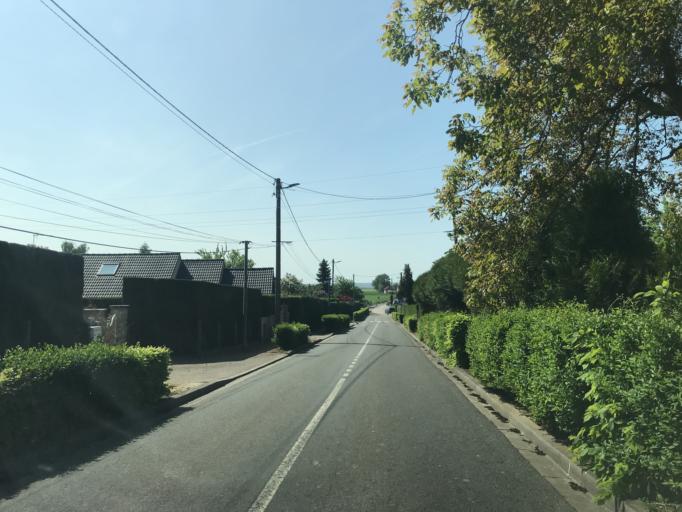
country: FR
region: Haute-Normandie
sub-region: Departement de la Seine-Maritime
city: Les Authieux-sur-le-Port-Saint-Ouen
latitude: 49.3592
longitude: 1.1523
